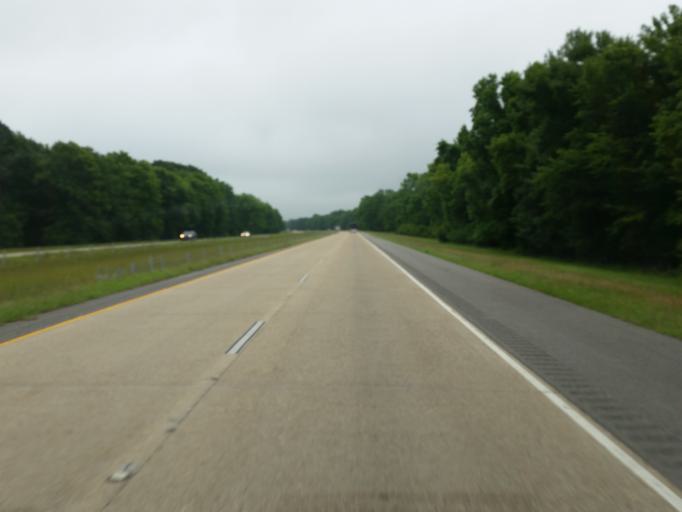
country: US
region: Louisiana
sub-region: Madison Parish
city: Tallulah
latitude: 32.3400
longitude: -91.0700
